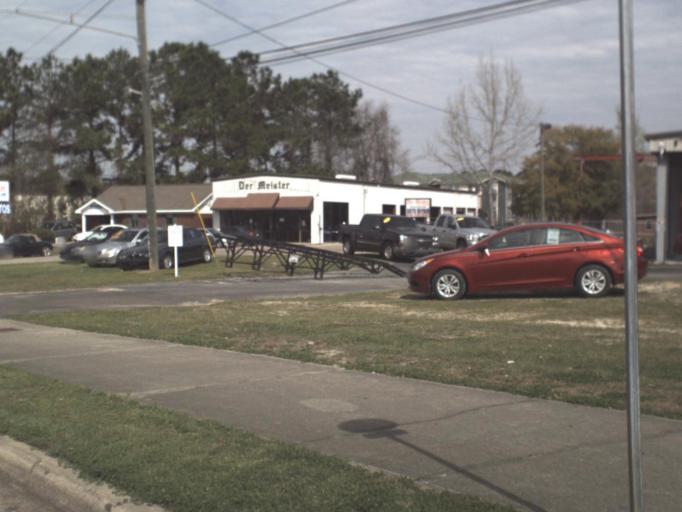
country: US
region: Florida
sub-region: Leon County
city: Tallahassee
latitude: 30.4481
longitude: -84.3279
